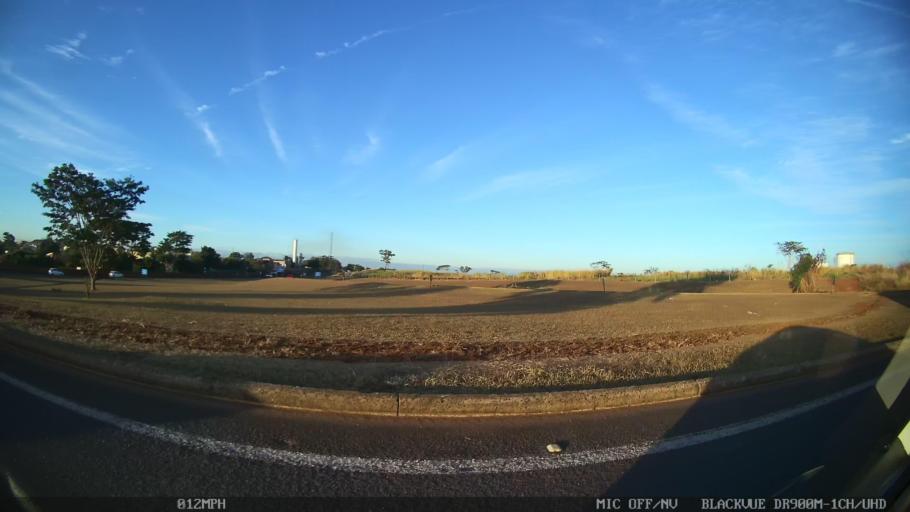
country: BR
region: Sao Paulo
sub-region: Catanduva
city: Catanduva
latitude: -21.1336
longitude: -49.0188
